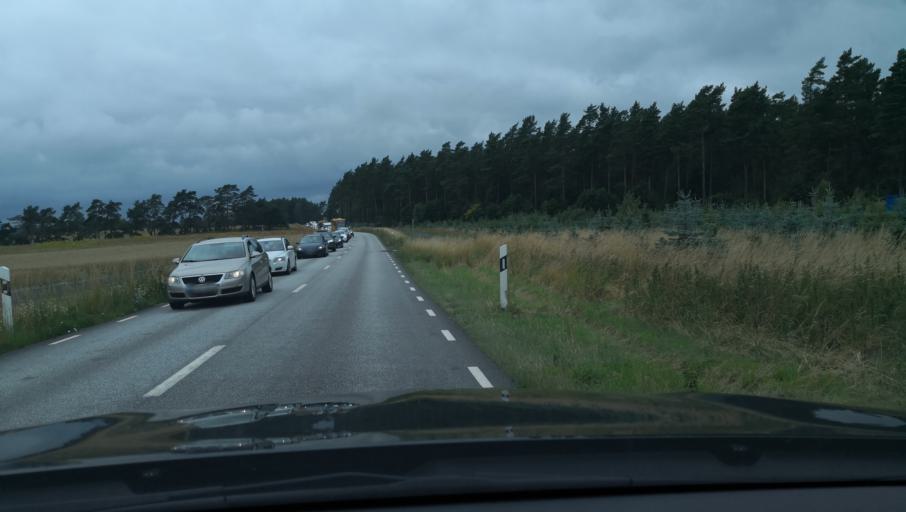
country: SE
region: Skane
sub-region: Simrishamns Kommun
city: Kivik
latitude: 55.7117
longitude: 14.1657
